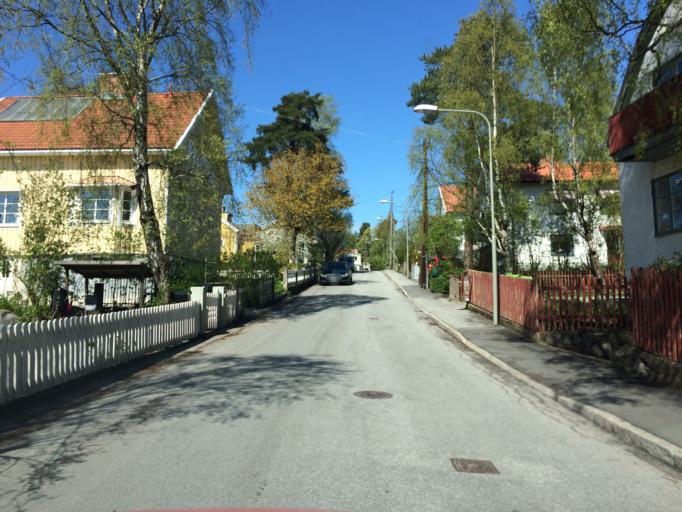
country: SE
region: Stockholm
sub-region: Huddinge Kommun
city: Segeltorp
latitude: 59.2913
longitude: 17.9536
